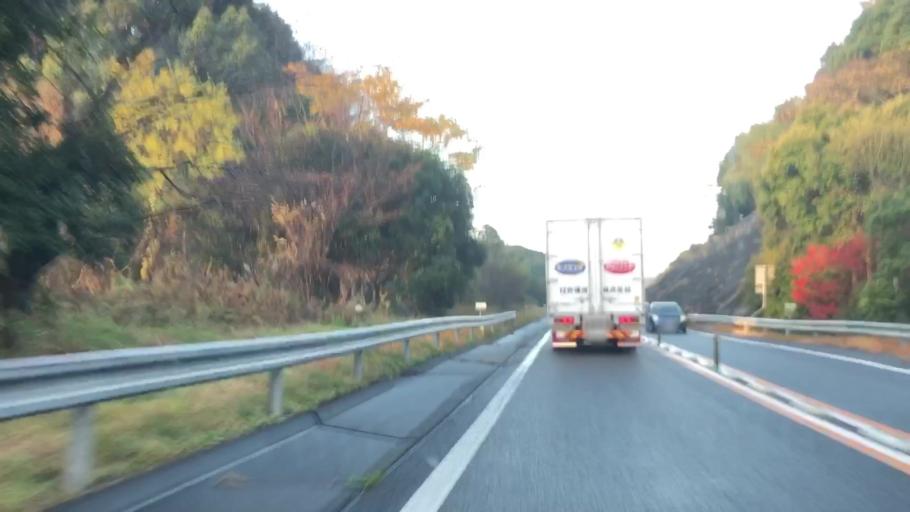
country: JP
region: Nagasaki
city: Sasebo
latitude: 33.1508
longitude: 129.7940
